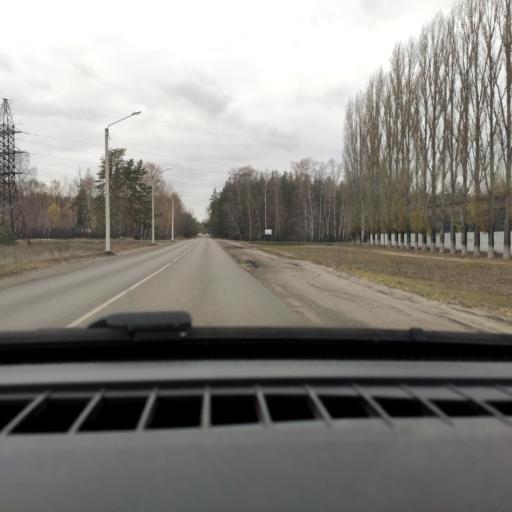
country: RU
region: Voronezj
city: Maslovka
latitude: 51.5770
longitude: 39.3015
